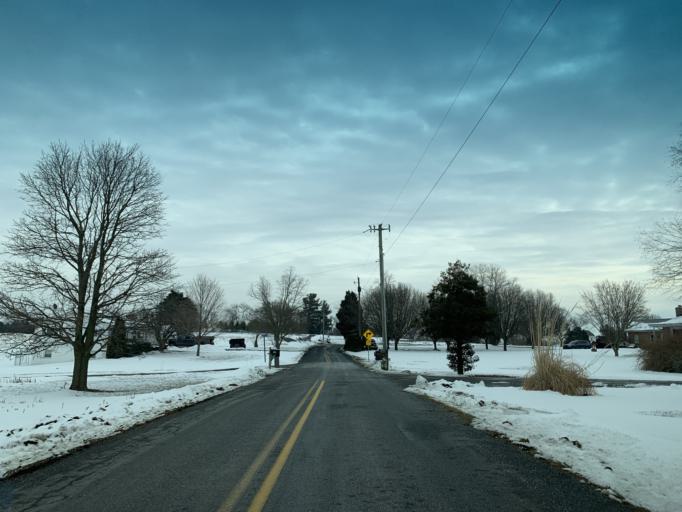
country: US
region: Pennsylvania
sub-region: York County
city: Susquehanna Trails
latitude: 39.7214
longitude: -76.2964
